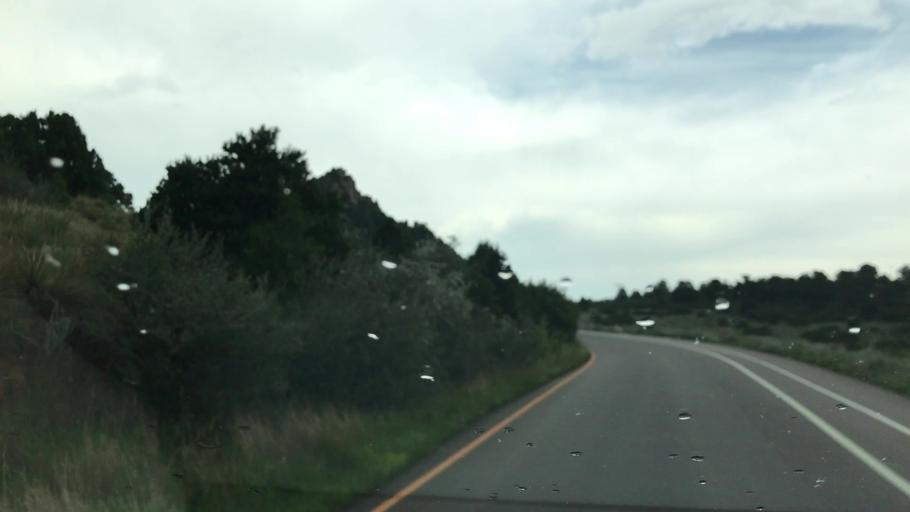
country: US
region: Colorado
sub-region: El Paso County
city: Manitou Springs
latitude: 38.8797
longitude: -104.8781
